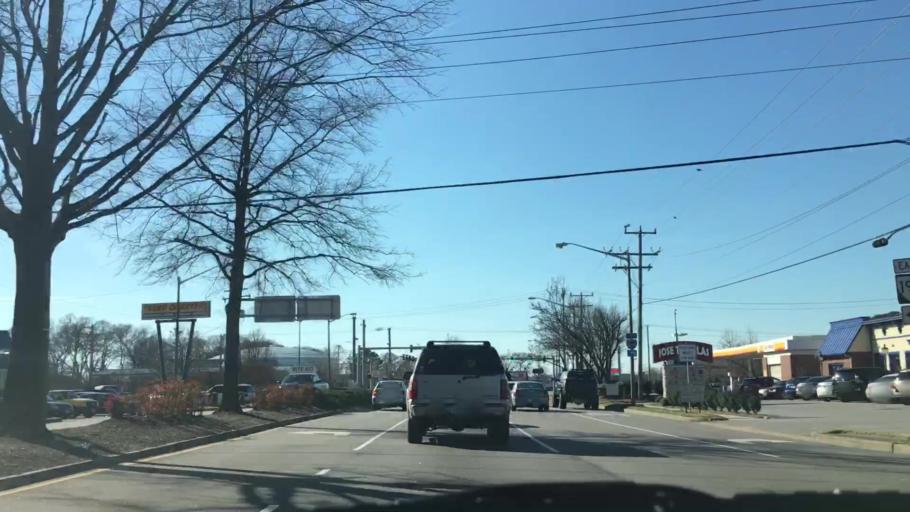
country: US
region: Virginia
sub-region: City of Norfolk
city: Norfolk
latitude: 36.9150
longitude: -76.2399
